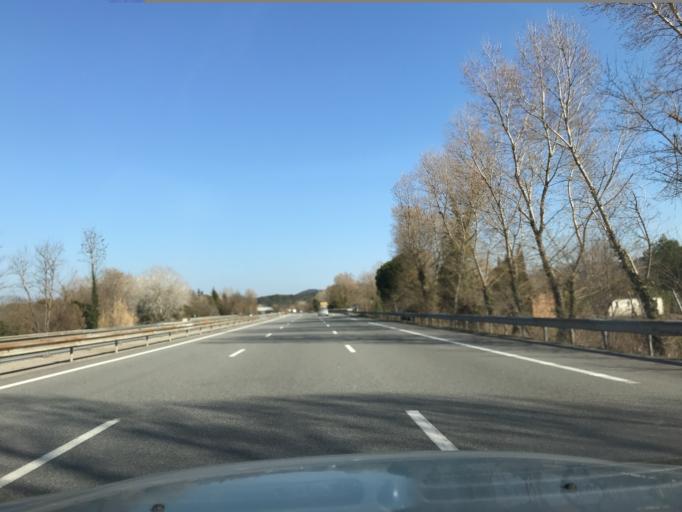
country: FR
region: Provence-Alpes-Cote d'Azur
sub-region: Departement du Var
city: Les Arcs
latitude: 43.4410
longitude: 6.4799
